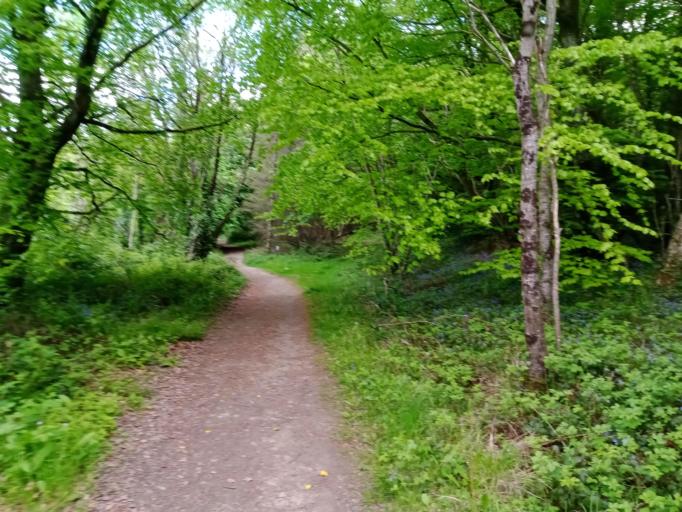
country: IE
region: Leinster
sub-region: Kilkenny
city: Castlecomer
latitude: 52.8183
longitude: -7.2053
